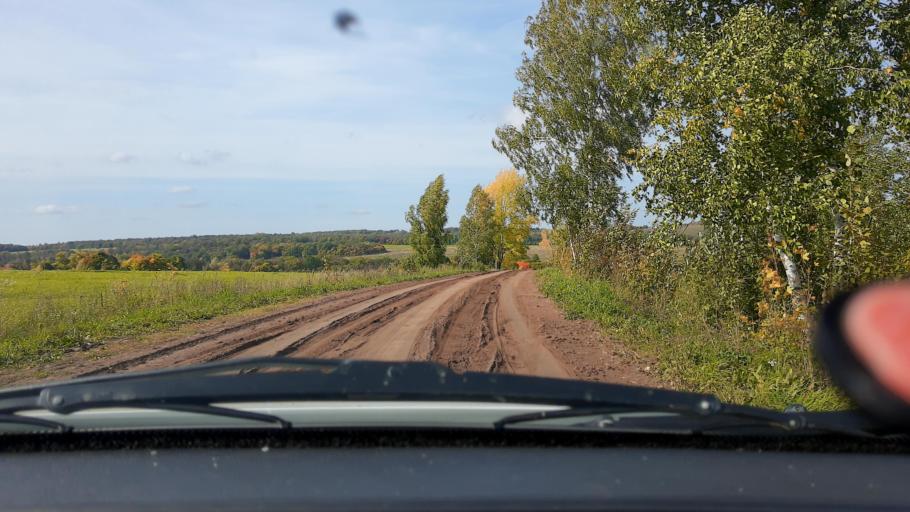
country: RU
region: Bashkortostan
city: Kudeyevskiy
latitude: 54.7124
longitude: 56.6413
